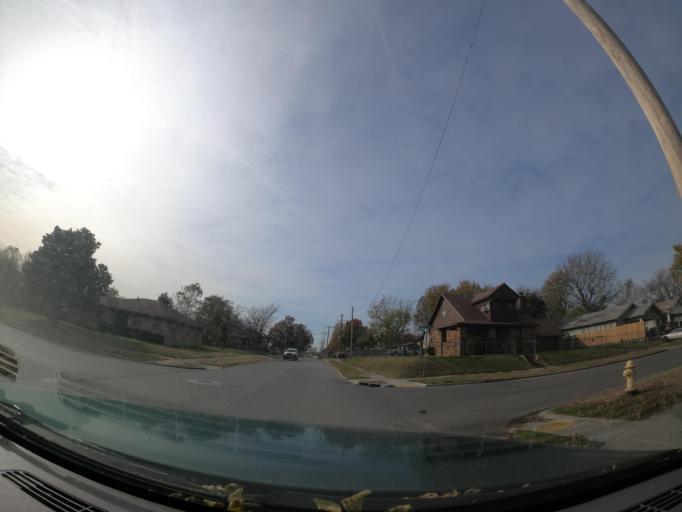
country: US
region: Oklahoma
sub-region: Tulsa County
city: Tulsa
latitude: 36.1627
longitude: -95.9645
